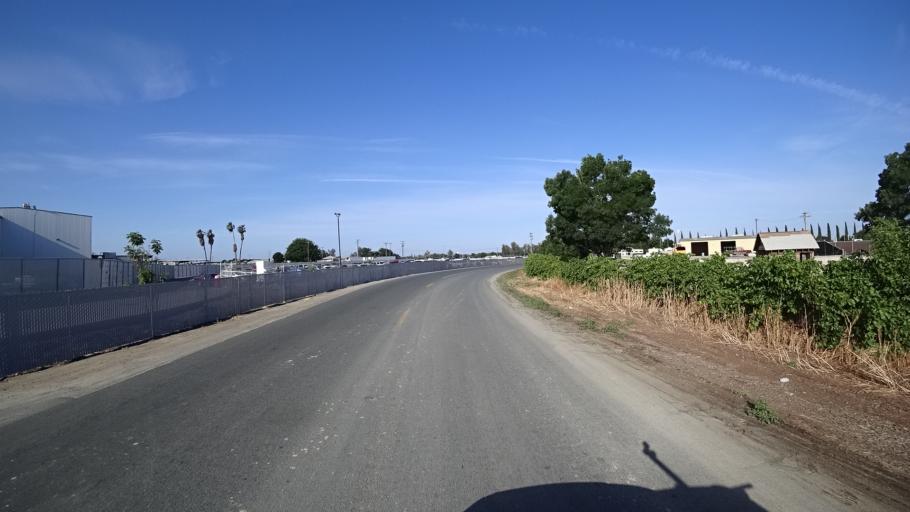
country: US
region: California
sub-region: Kings County
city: Home Garden
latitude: 36.3234
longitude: -119.6154
